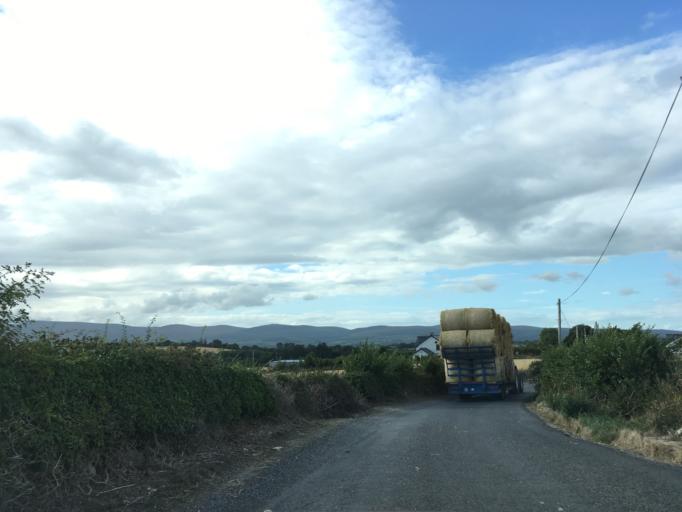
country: IE
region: Munster
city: Cahir
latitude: 52.3032
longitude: -7.9460
